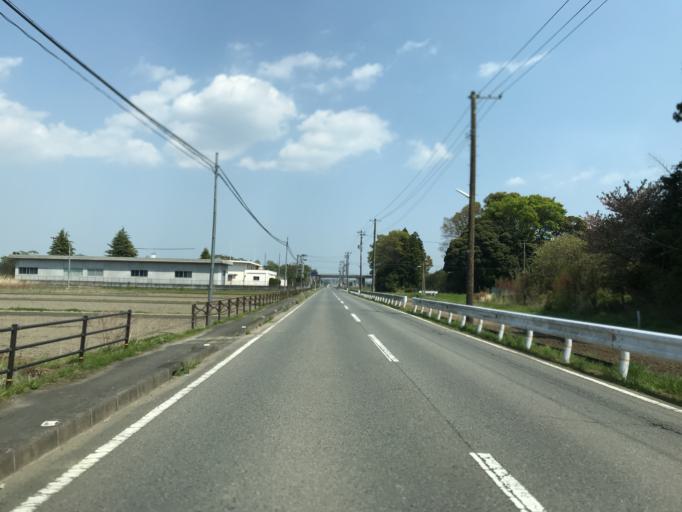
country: JP
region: Ibaraki
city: Kitaibaraki
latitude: 36.9179
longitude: 140.7540
